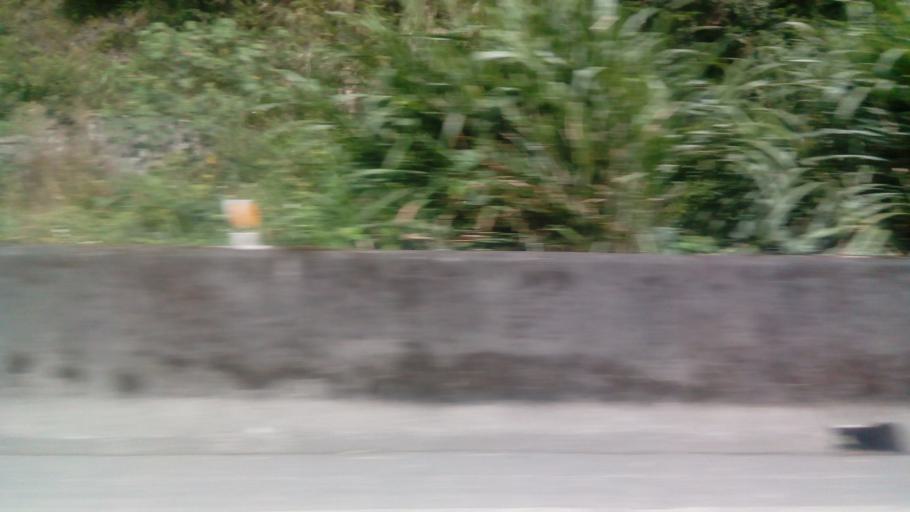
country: TW
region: Taiwan
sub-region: Yilan
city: Yilan
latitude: 24.5598
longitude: 121.4772
